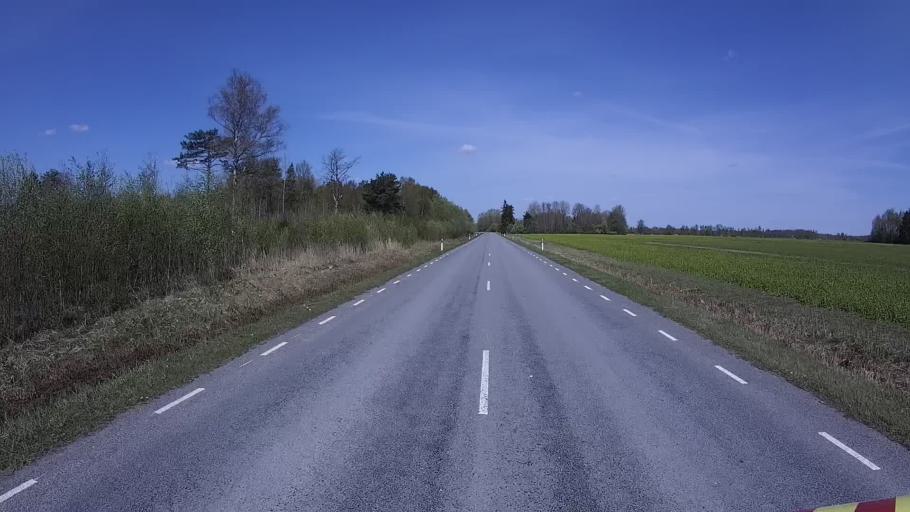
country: EE
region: Laeaene
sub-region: Ridala Parish
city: Uuemoisa
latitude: 58.8518
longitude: 23.6392
